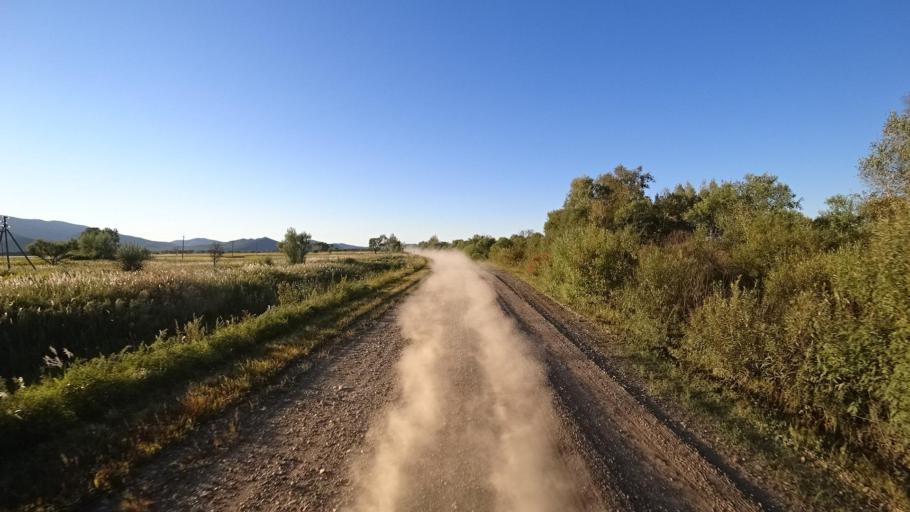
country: RU
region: Primorskiy
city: Kirovskiy
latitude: 44.8023
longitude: 133.6206
